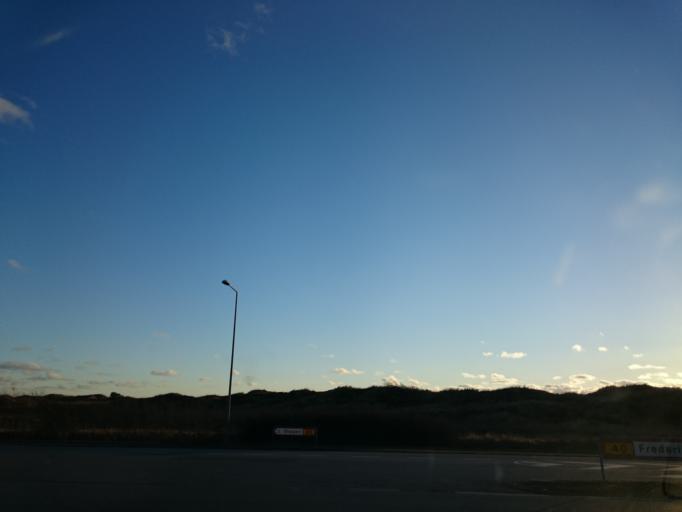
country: DK
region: North Denmark
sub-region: Frederikshavn Kommune
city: Skagen
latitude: 57.7267
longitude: 10.5515
